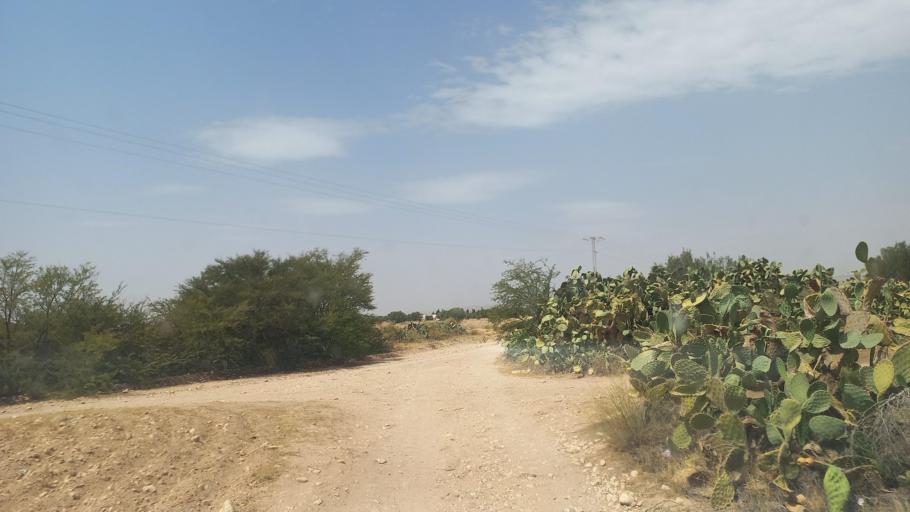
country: TN
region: Al Qasrayn
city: Kasserine
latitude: 35.2563
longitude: 9.0061
